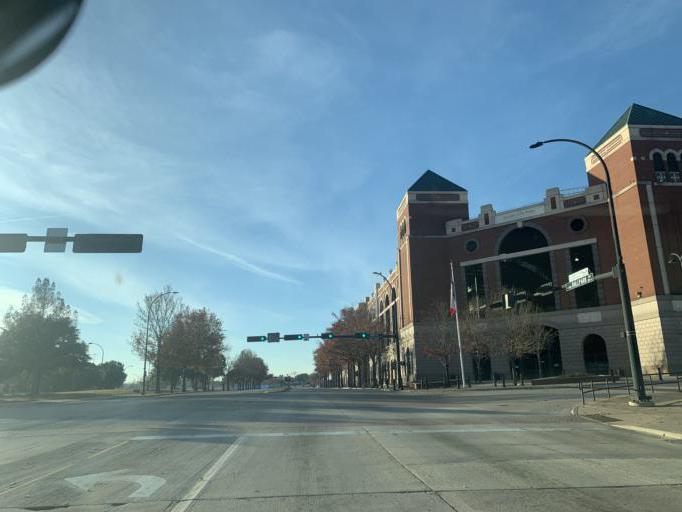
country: US
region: Texas
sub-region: Tarrant County
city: Arlington
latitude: 32.7528
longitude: -97.0811
